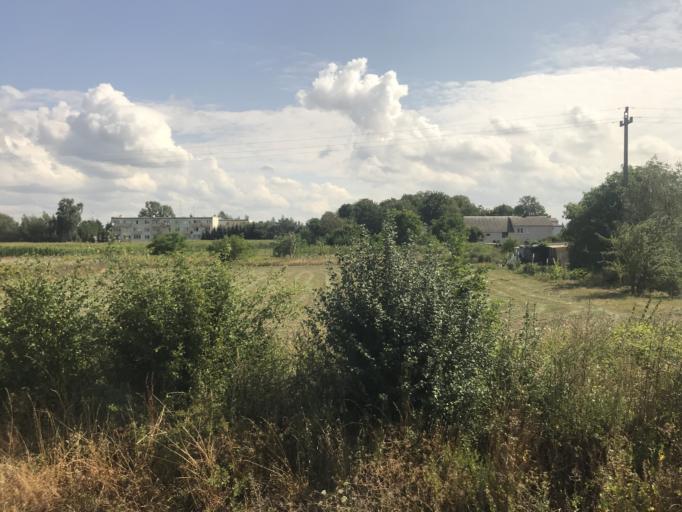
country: PL
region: Kujawsko-Pomorskie
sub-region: Powiat inowroclawski
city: Zlotniki Kujawskie
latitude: 52.9098
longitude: 18.1407
